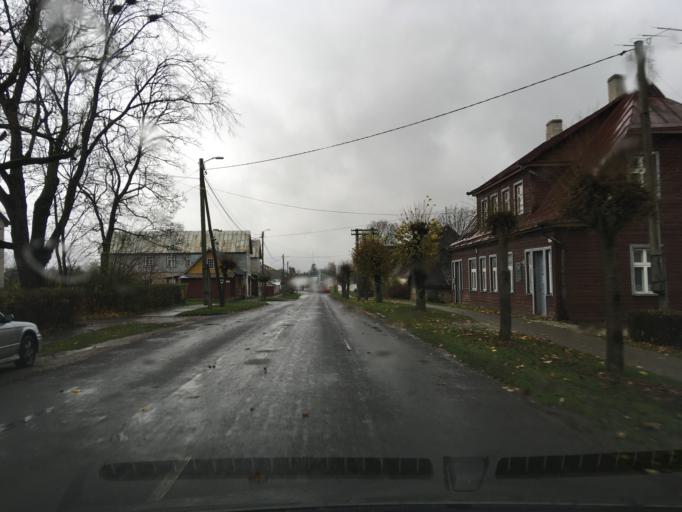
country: EE
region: Laeaene
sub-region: Lihula vald
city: Lihula
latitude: 58.6907
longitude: 23.8367
